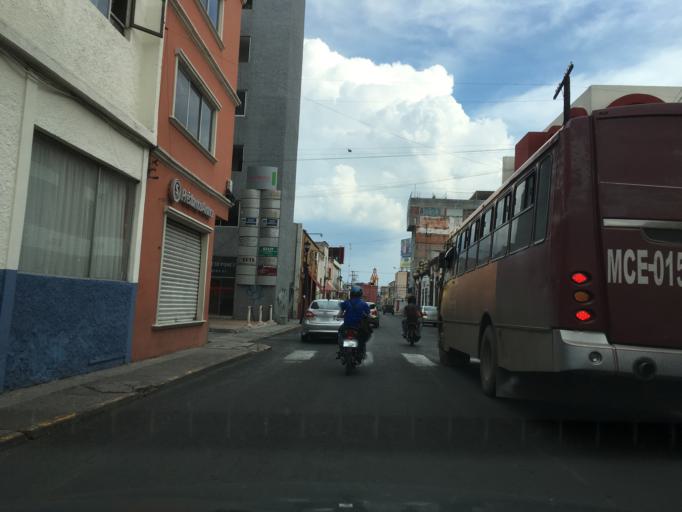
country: MX
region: Guanajuato
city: Celaya
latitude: 20.5209
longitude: -100.8153
